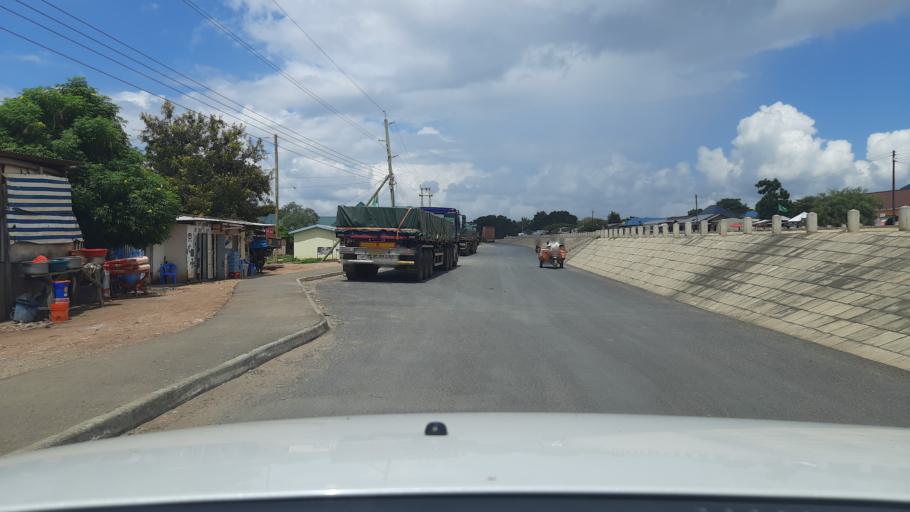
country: TZ
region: Arusha
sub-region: Longido District
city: Longido
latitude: -2.7336
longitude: 36.6971
